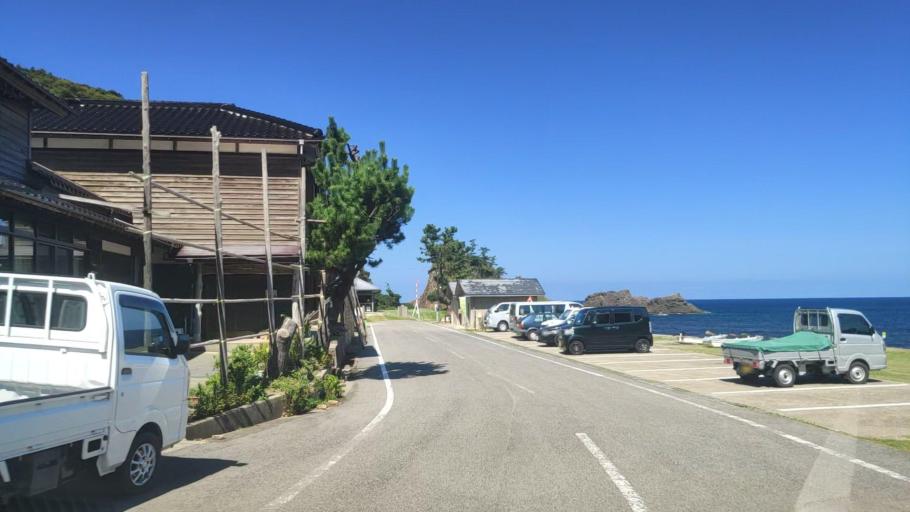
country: JP
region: Ishikawa
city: Nanao
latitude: 37.5282
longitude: 137.2646
